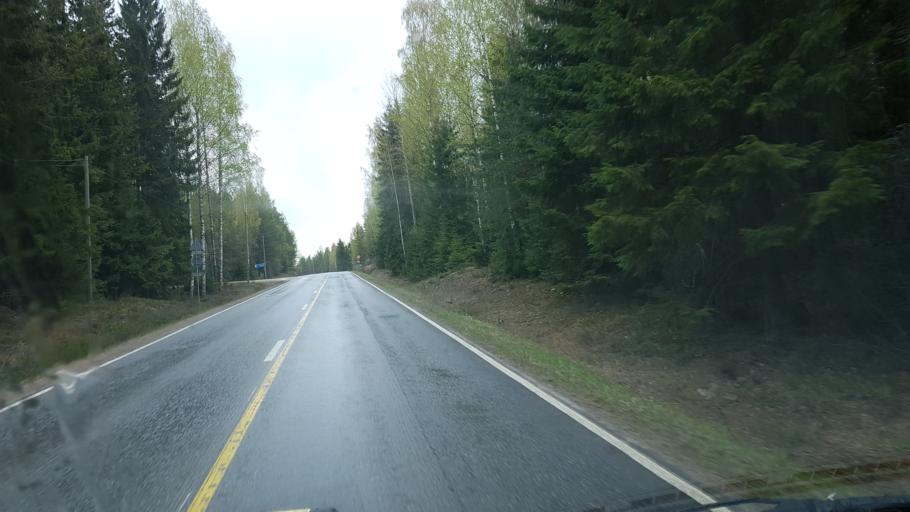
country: FI
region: Pirkanmaa
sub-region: Tampere
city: Pirkkala
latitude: 61.3947
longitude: 23.6249
